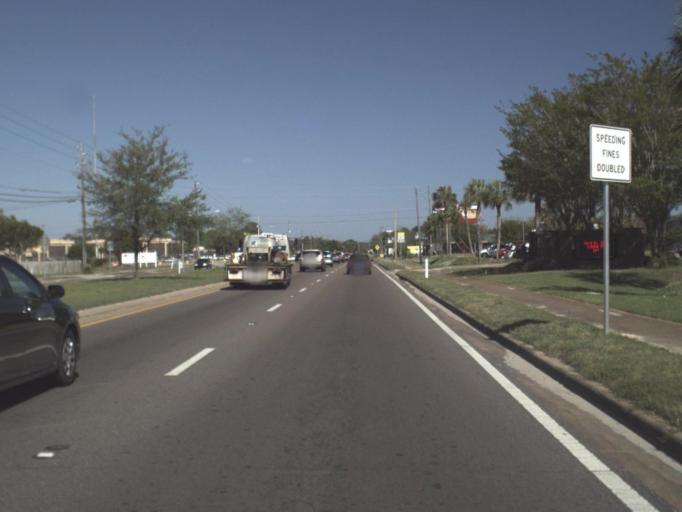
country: US
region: Florida
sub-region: Okaloosa County
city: Ocean City
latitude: 30.4492
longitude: -86.6233
